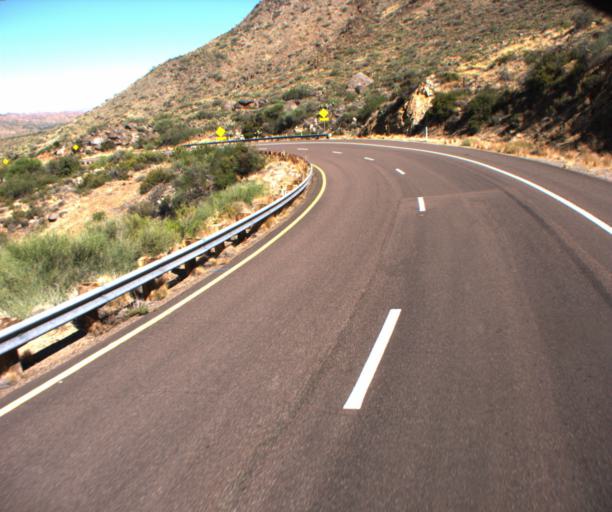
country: US
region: Arizona
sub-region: Yavapai County
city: Congress
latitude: 34.2075
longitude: -112.7986
